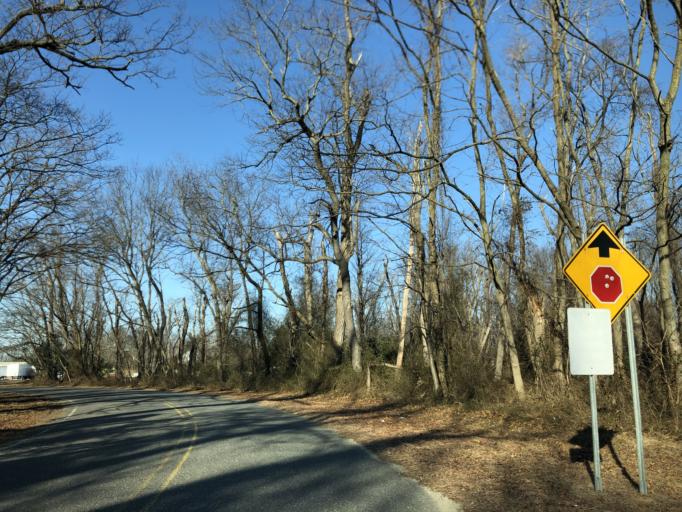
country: US
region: New Jersey
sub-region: Gloucester County
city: Beckett
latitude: 39.7936
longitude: -75.3524
